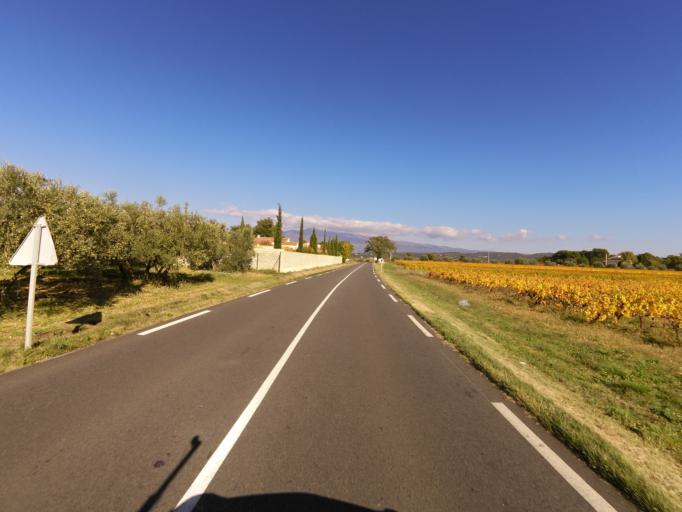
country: FR
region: Provence-Alpes-Cote d'Azur
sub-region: Departement du Vaucluse
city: Caromb
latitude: 44.0875
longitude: 5.1232
